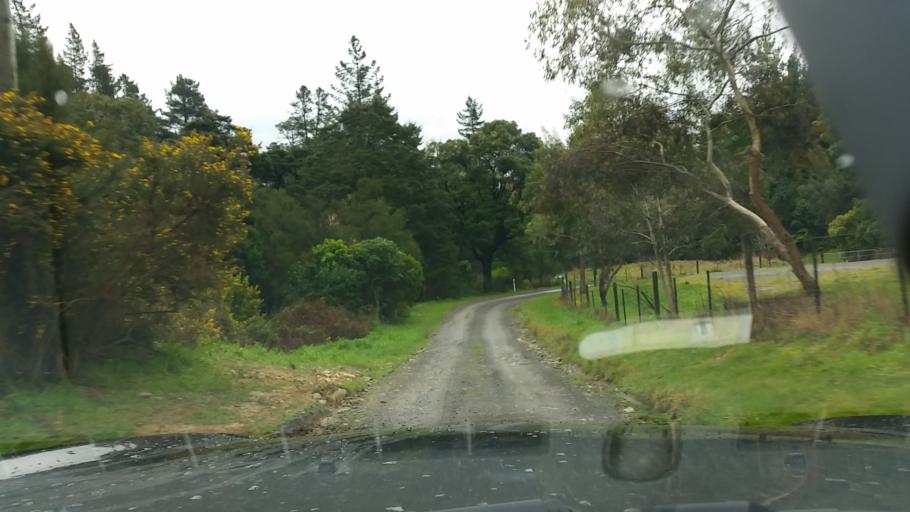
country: NZ
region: Marlborough
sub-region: Marlborough District
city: Picton
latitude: -41.2894
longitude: 174.0394
